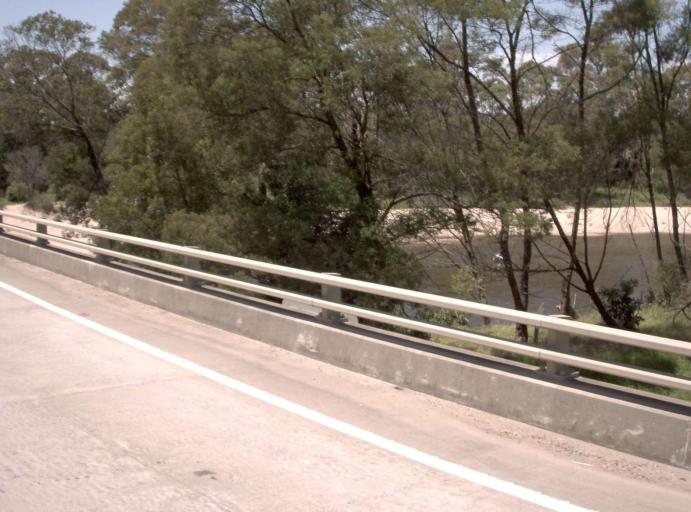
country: AU
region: Victoria
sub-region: East Gippsland
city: Lakes Entrance
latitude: -37.7164
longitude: 148.4534
